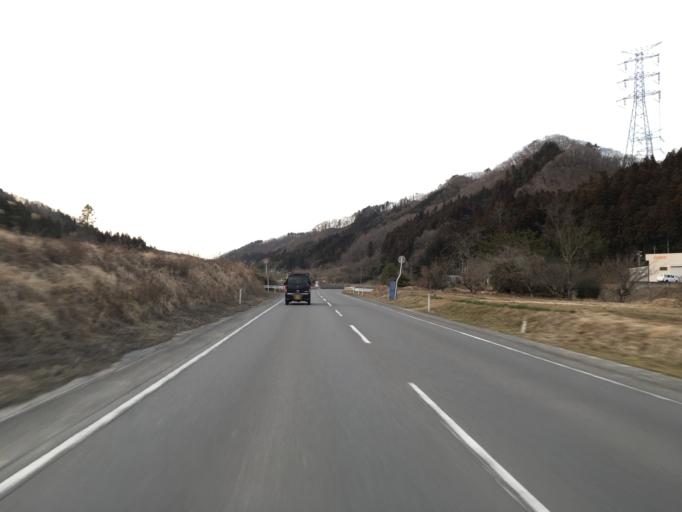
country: JP
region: Fukushima
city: Ishikawa
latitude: 37.0292
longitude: 140.3566
